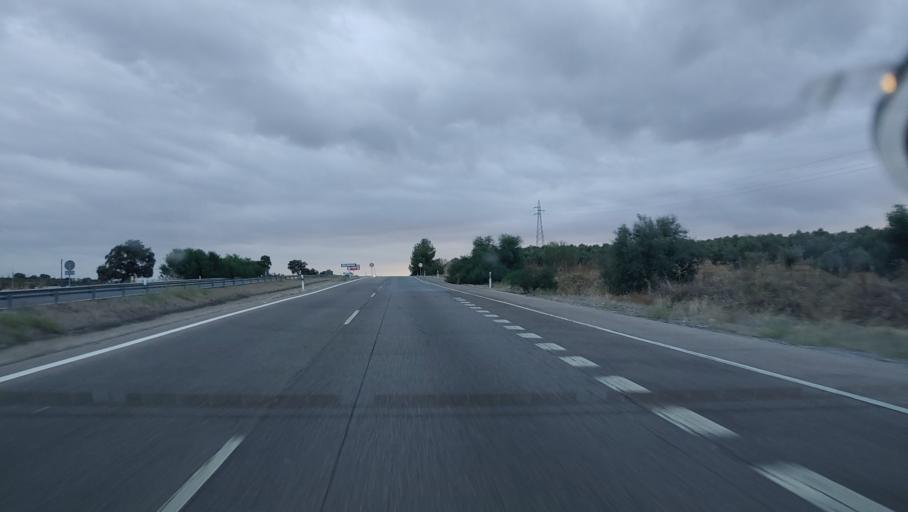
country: ES
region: Andalusia
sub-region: Provincia de Jaen
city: Guarroman
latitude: 38.1568
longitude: -3.7164
